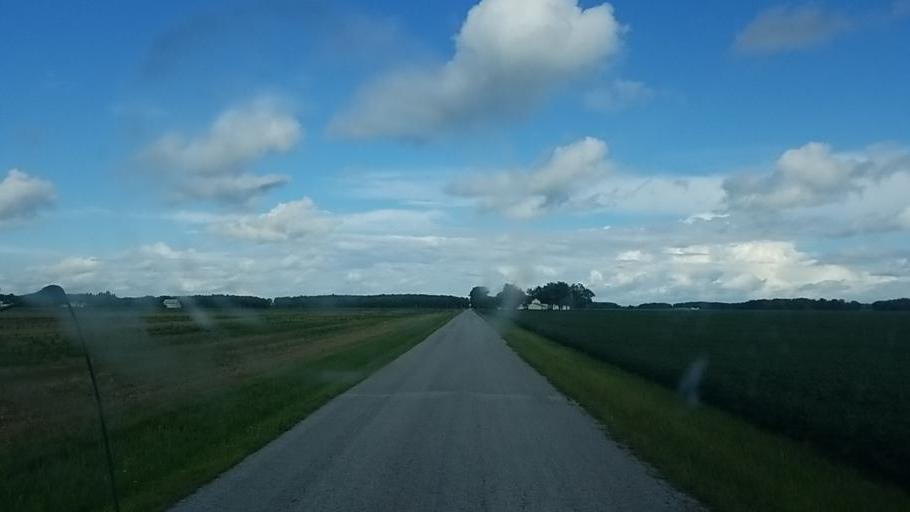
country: US
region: Ohio
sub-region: Hardin County
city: Forest
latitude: 40.7598
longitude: -83.4854
